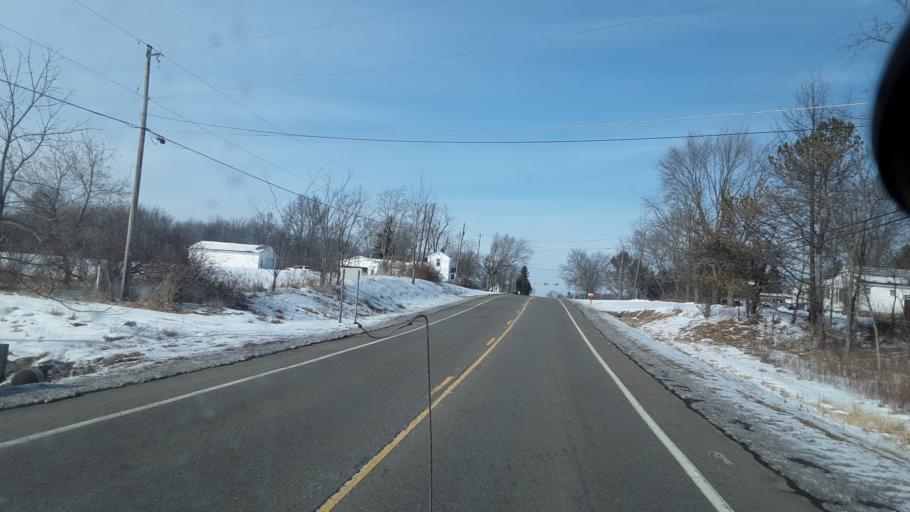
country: US
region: Ohio
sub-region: Stark County
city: Alliance
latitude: 41.0287
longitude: -81.1480
